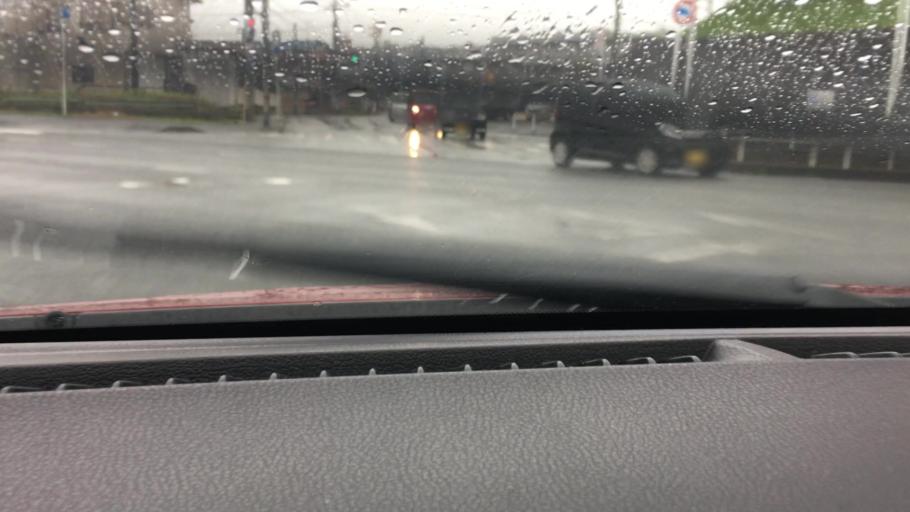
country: JP
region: Chiba
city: Kisarazu
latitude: 35.3743
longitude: 139.9377
